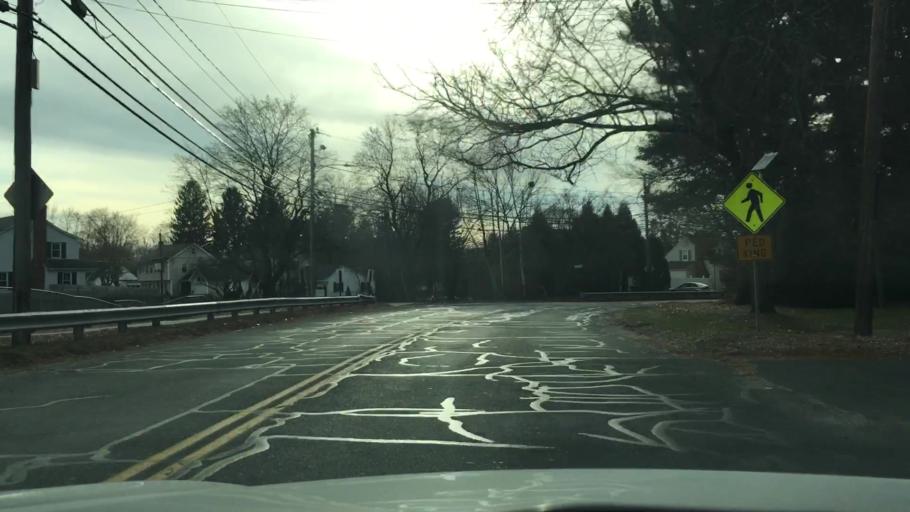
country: US
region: Massachusetts
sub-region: Hampden County
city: Westfield
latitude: 42.1131
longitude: -72.7544
